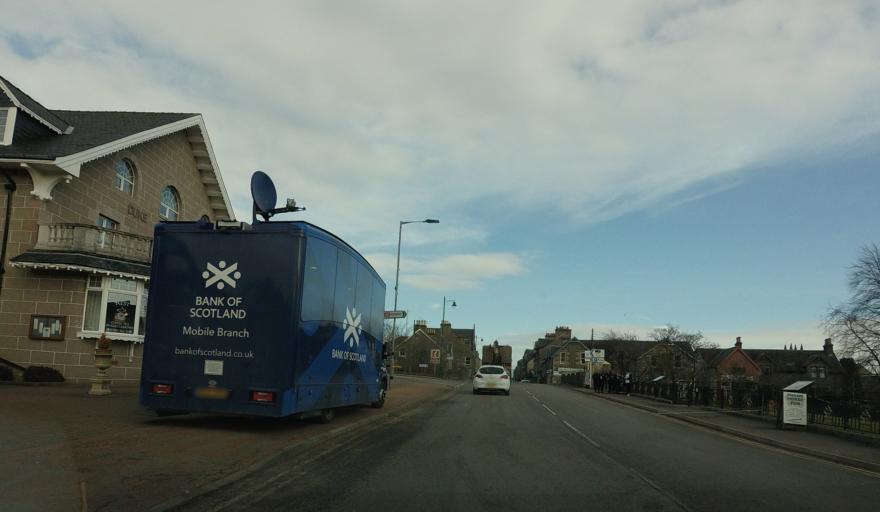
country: GB
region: Scotland
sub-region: Highland
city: Kingussie
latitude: 57.0797
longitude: -4.0536
